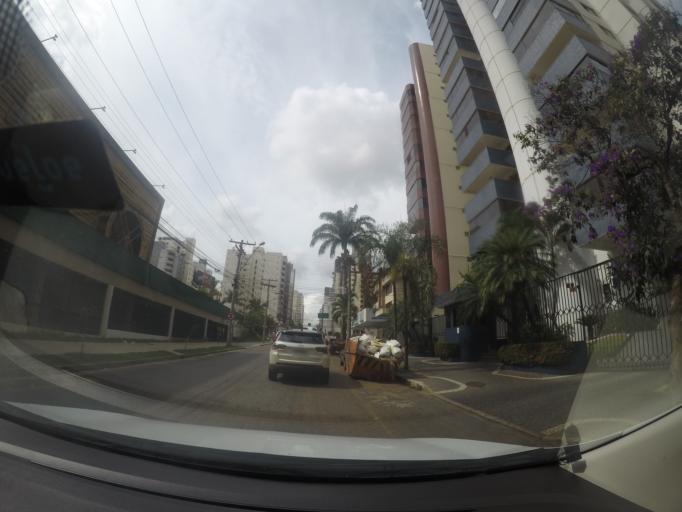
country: BR
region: Goias
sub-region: Goiania
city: Goiania
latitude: -16.7134
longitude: -49.2691
